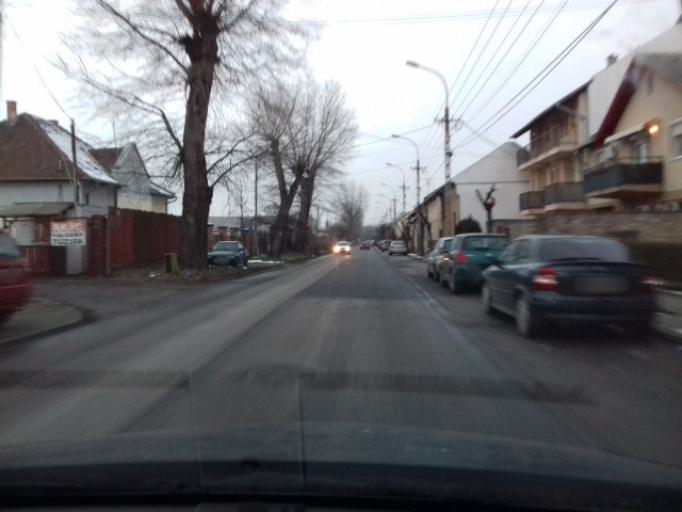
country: HU
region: Budapest
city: Budapest XV. keruelet
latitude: 47.5588
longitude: 19.1109
